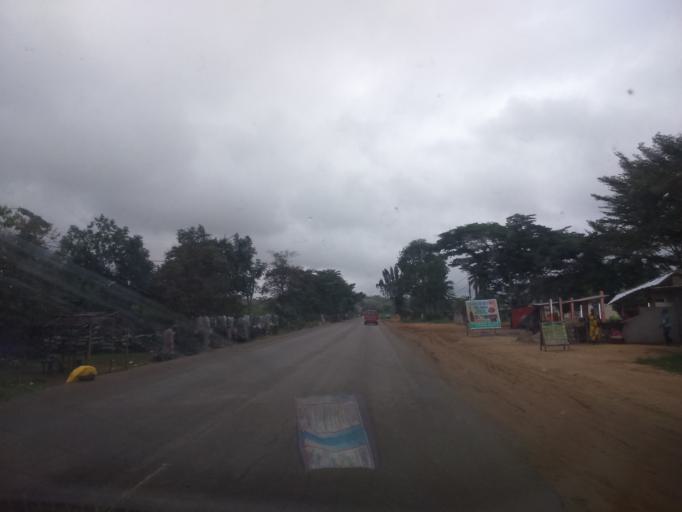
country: CI
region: Sud-Comoe
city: Bonoua
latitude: 5.2464
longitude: -3.6235
